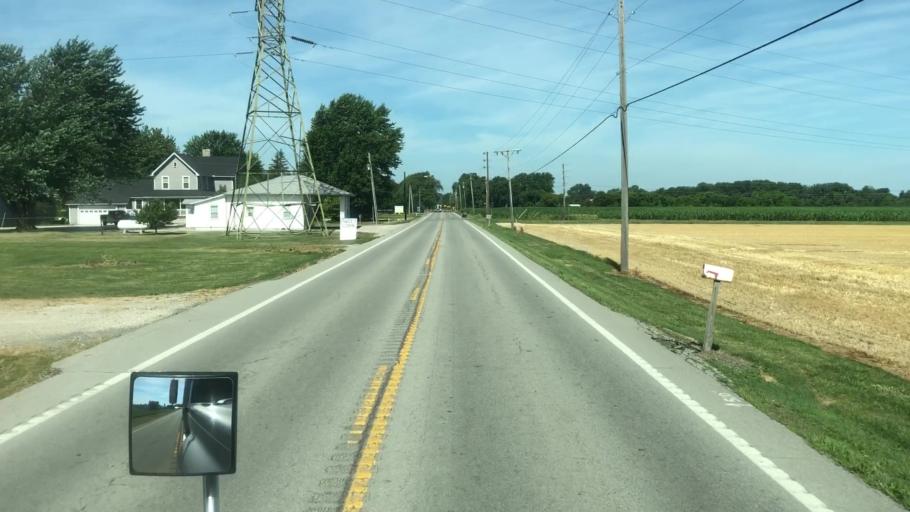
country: US
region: Ohio
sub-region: Erie County
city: Sandusky
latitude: 41.4419
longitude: -82.8009
